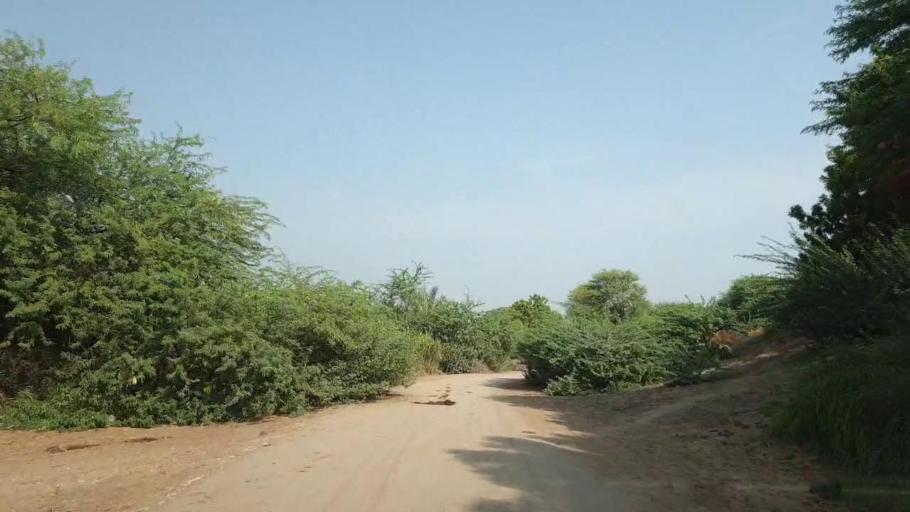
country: PK
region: Sindh
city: Larkana
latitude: 27.4805
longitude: 68.2555
